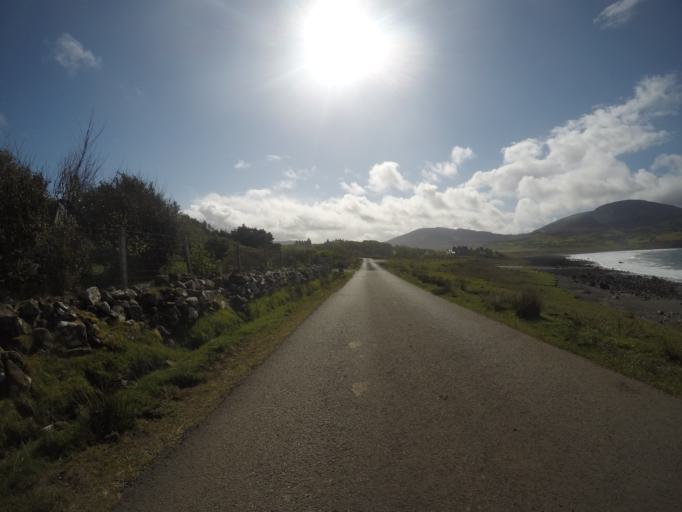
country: GB
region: Scotland
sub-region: Highland
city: Portree
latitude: 57.6349
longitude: -6.2115
